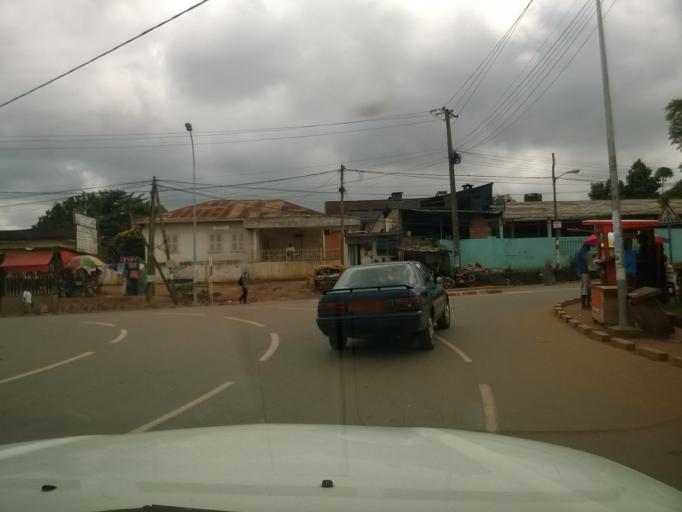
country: CM
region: Centre
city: Yaounde
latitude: 3.8399
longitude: 11.4961
